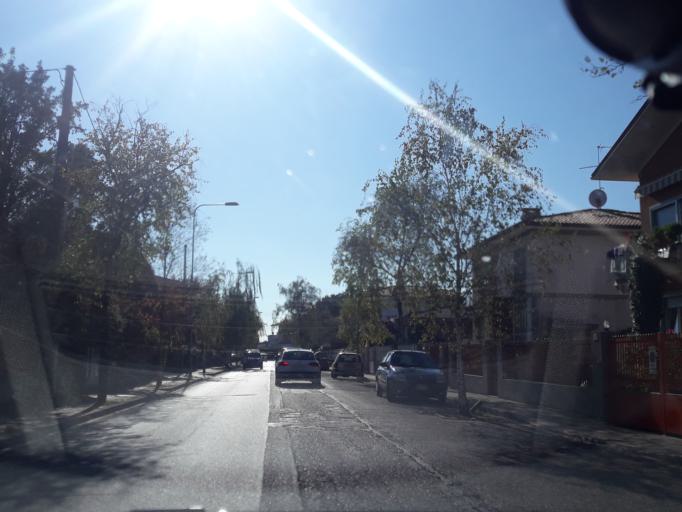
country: IT
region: Friuli Venezia Giulia
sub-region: Provincia di Udine
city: Udine
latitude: 46.0860
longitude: 13.2423
